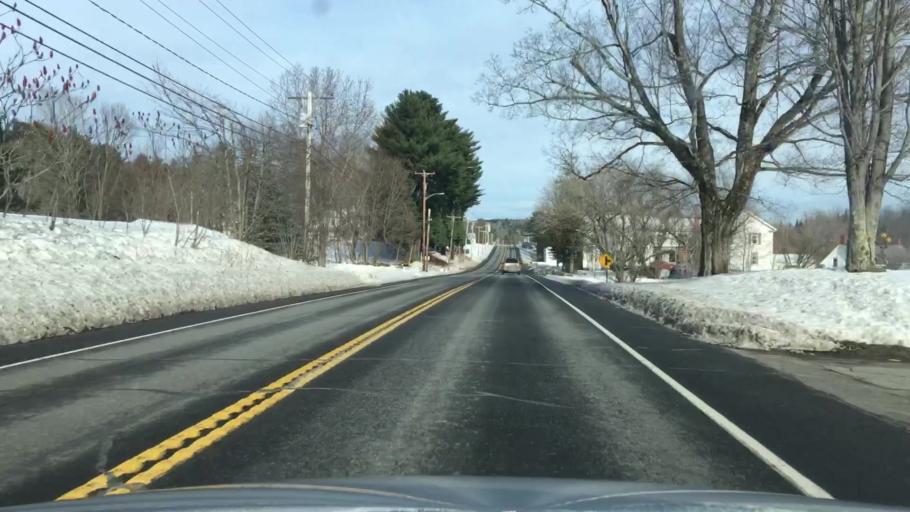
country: US
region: Maine
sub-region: Androscoggin County
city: Greene
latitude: 44.1776
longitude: -70.1689
